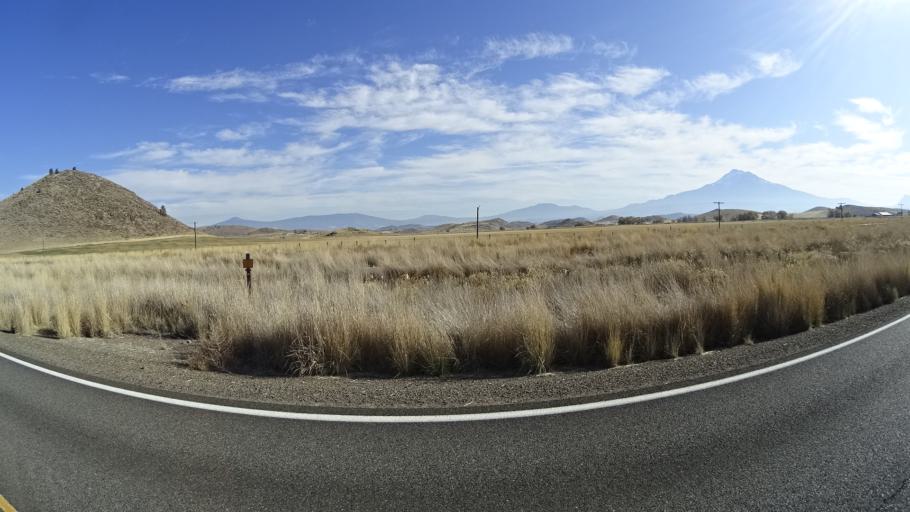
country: US
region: California
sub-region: Siskiyou County
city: Weed
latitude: 41.5307
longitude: -122.5239
